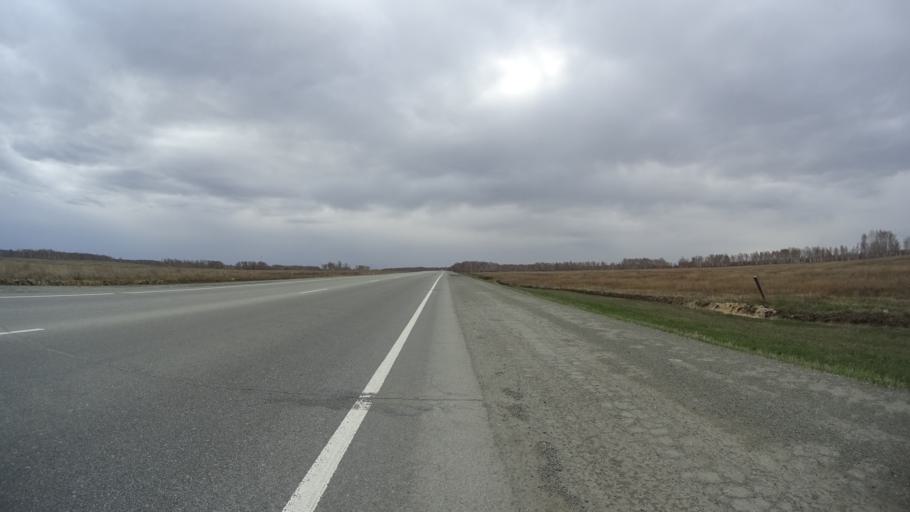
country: RU
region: Chelyabinsk
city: Yemanzhelinsk
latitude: 54.7047
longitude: 61.2557
